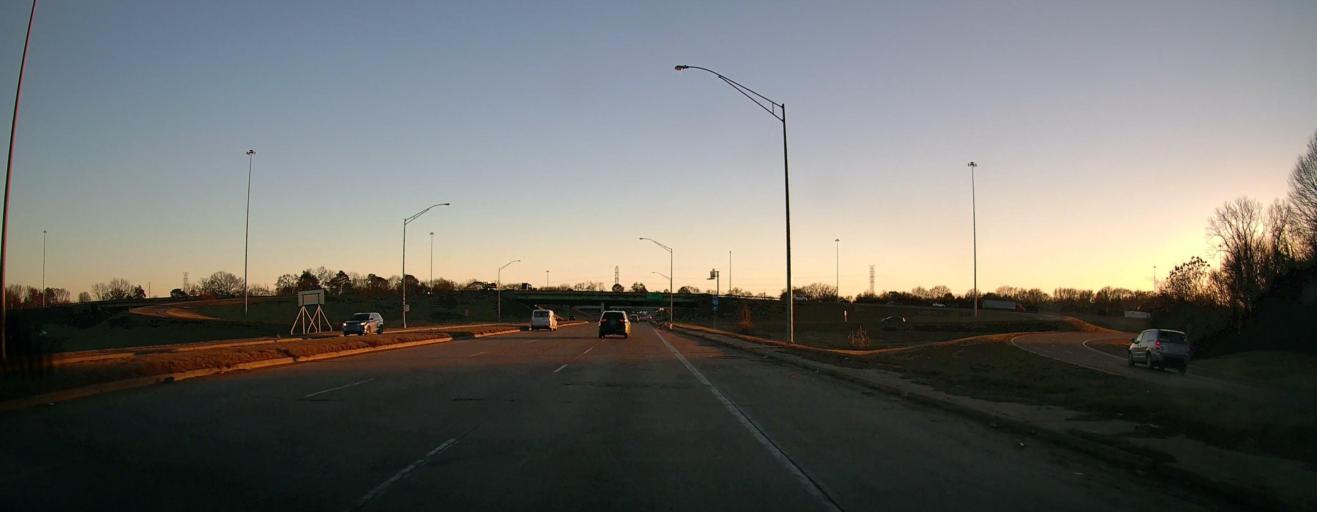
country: US
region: Tennessee
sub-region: Shelby County
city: Bartlett
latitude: 35.1953
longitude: -89.9258
